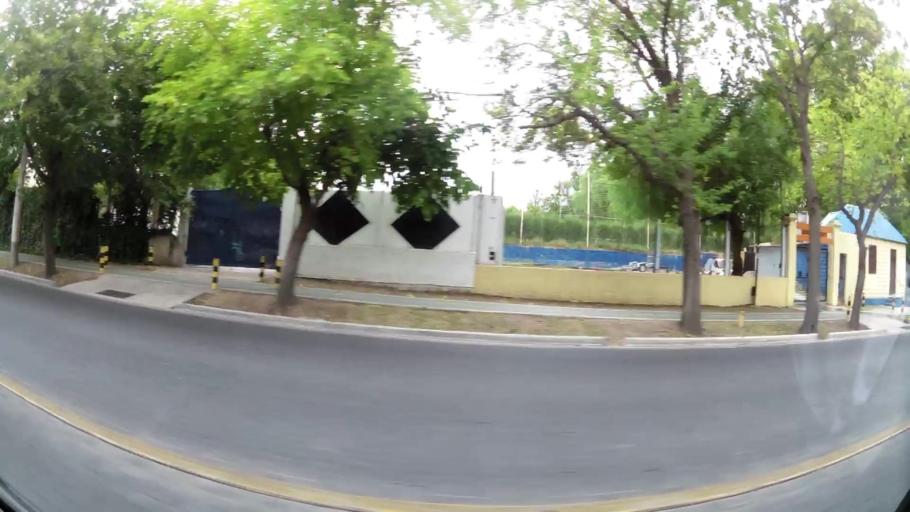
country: AR
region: Mendoza
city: Mendoza
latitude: -32.8902
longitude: -68.8619
